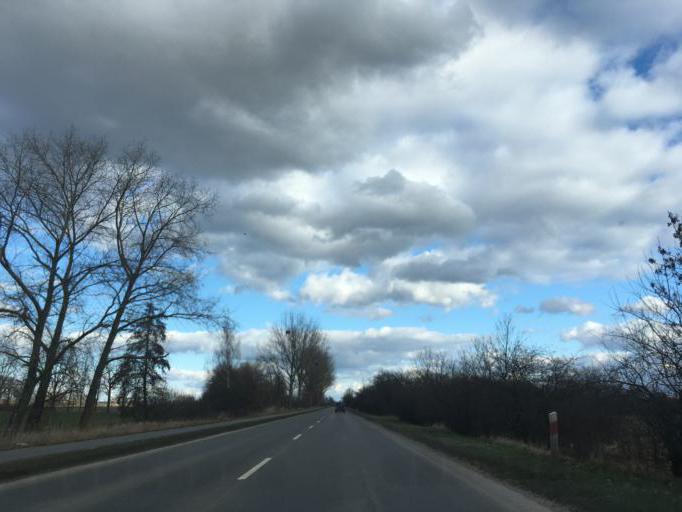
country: PL
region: Pomeranian Voivodeship
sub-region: Gdansk
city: Gdansk
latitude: 54.3275
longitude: 18.7542
